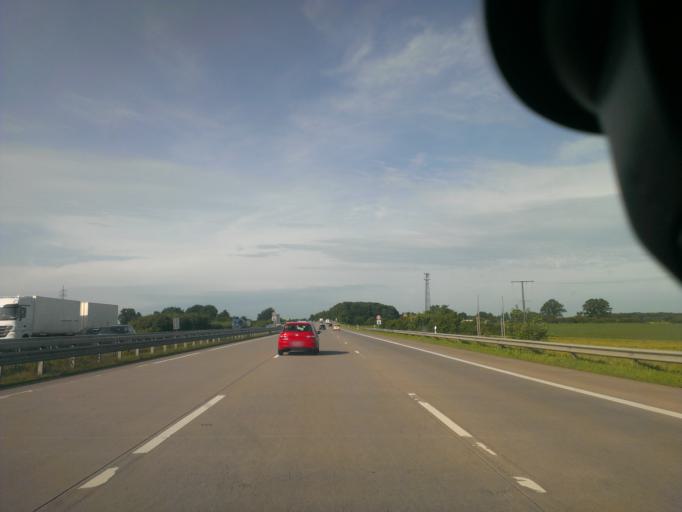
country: DE
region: Schleswig-Holstein
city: Politz
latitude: 53.7670
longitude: 10.3897
